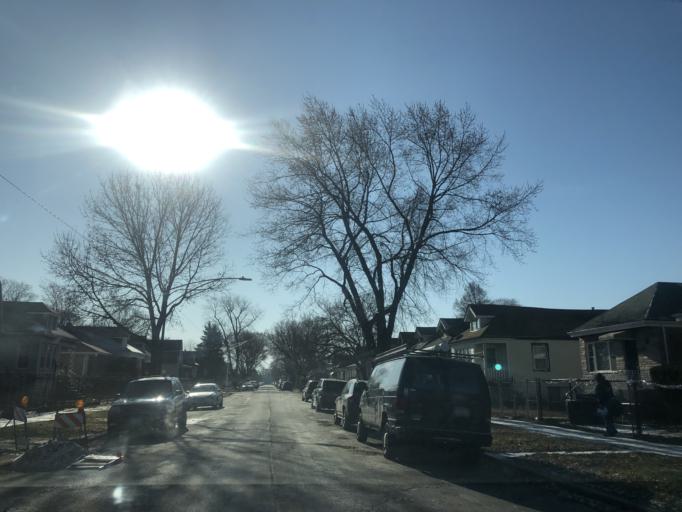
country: US
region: Illinois
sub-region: Cook County
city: Evergreen Park
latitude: 41.7639
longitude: -87.6711
